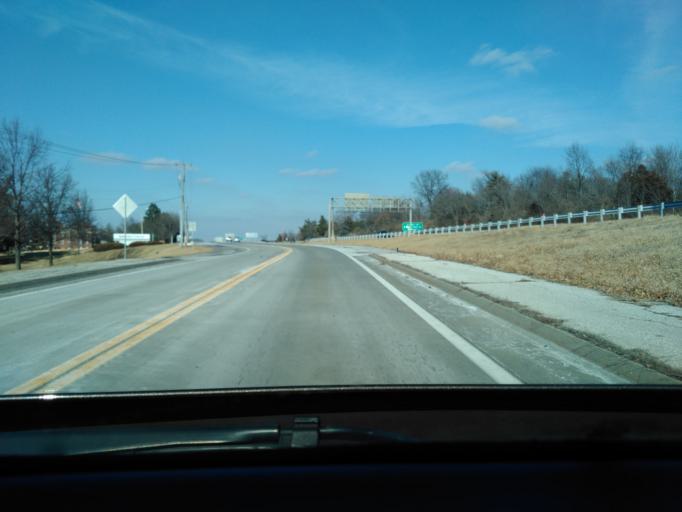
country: US
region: Missouri
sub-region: Saint Louis County
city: Manchester
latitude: 38.6292
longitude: -90.5151
